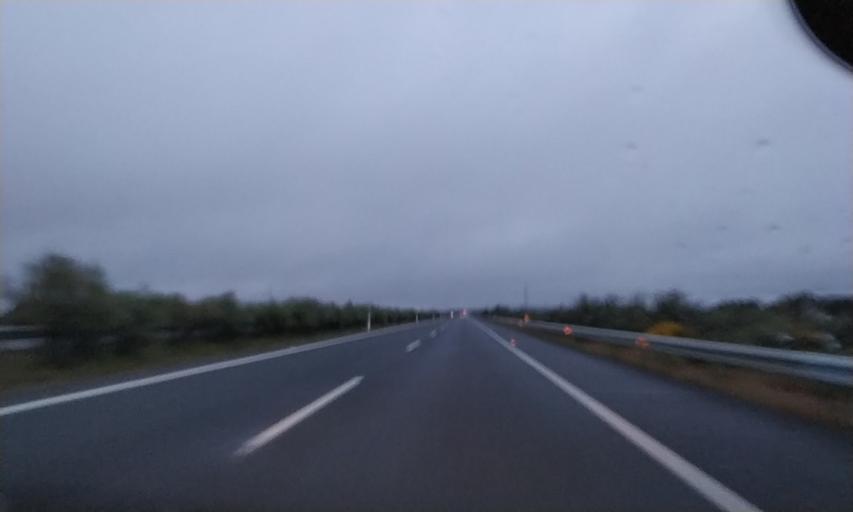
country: ES
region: Extremadura
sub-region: Provincia de Badajoz
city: Carmonita
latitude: 39.1139
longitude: -6.2798
